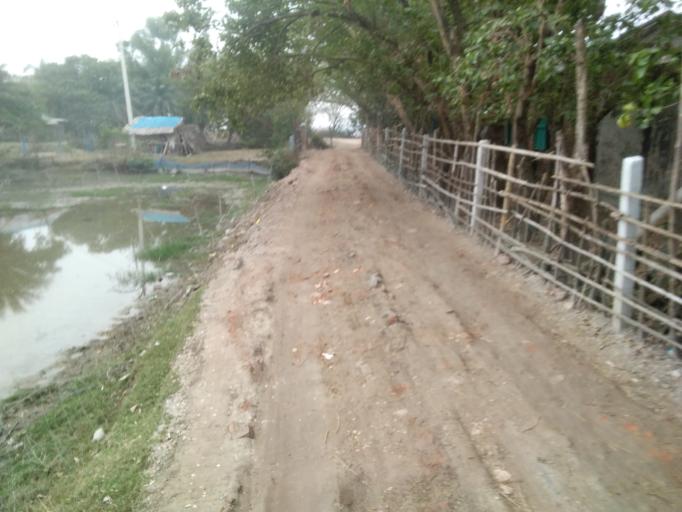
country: BD
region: Khulna
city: Satkhira
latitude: 22.5721
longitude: 89.0770
